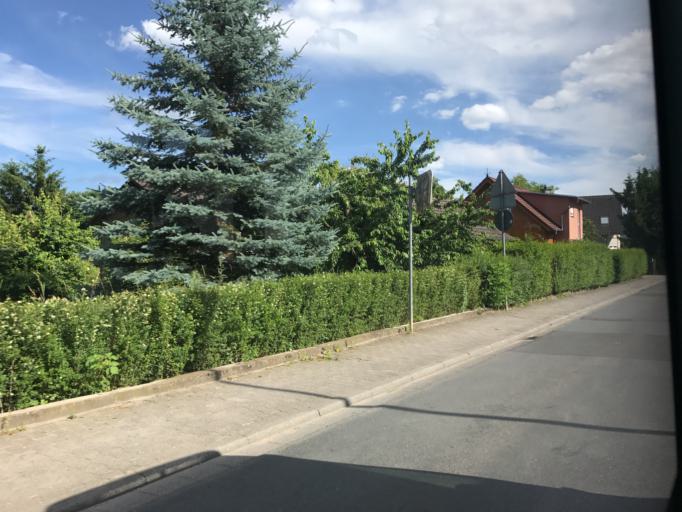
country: DE
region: Hesse
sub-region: Regierungsbezirk Darmstadt
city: Eltville
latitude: 50.0364
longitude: 8.1169
